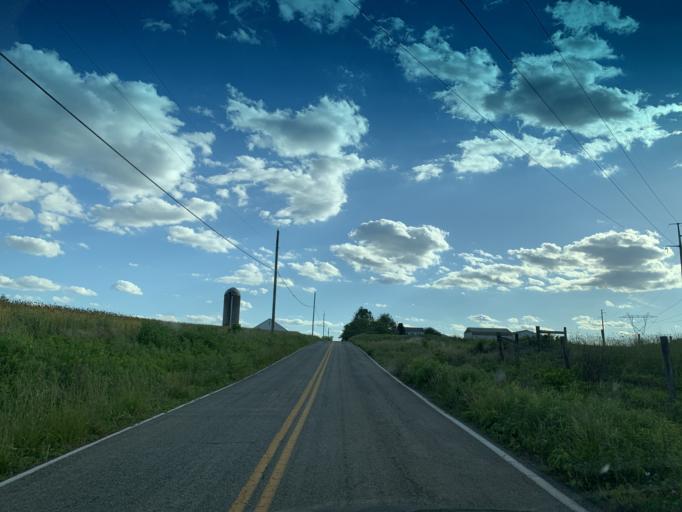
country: US
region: Maryland
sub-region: Cecil County
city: Rising Sun
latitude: 39.6708
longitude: -75.9994
